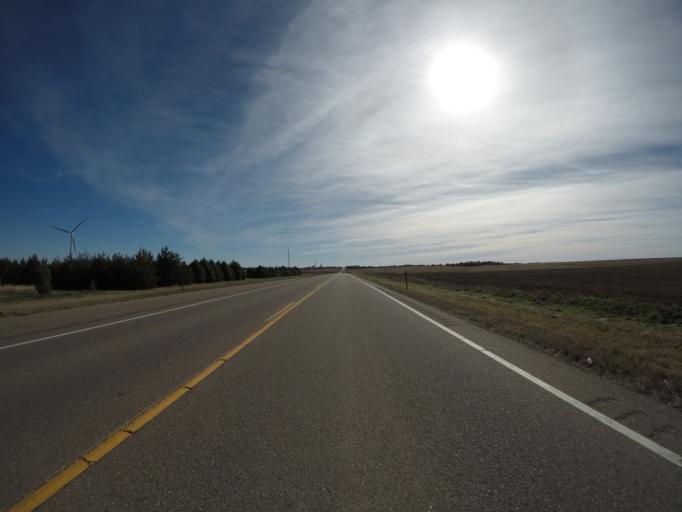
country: US
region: Colorado
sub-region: Kit Carson County
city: Burlington
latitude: 39.3465
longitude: -102.2598
